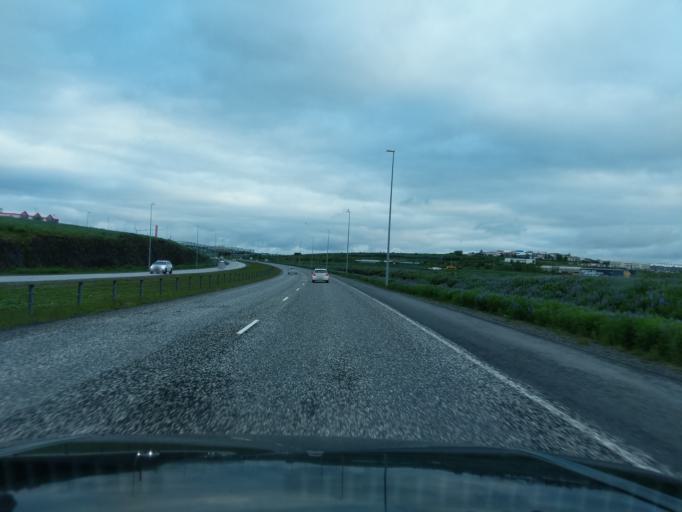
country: IS
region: Capital Region
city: Mosfellsbaer
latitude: 64.1439
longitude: -21.7546
